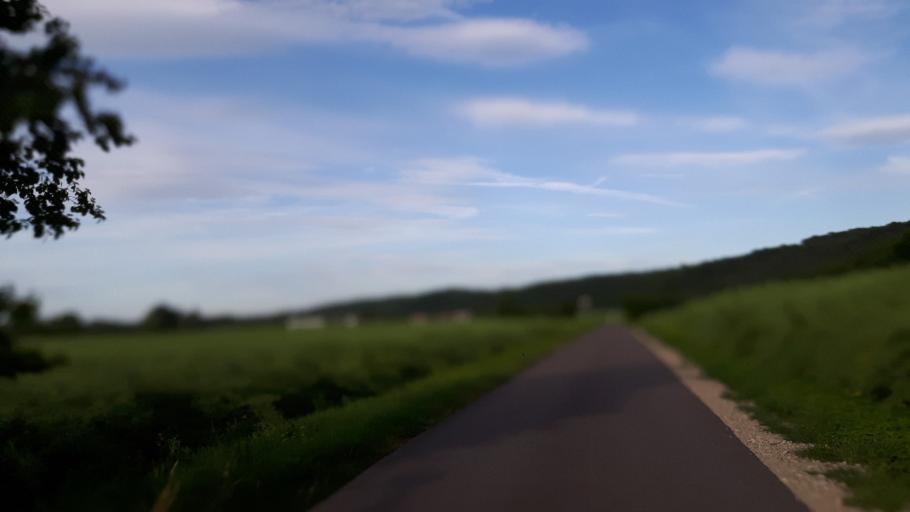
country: DE
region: Saxony-Anhalt
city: Leissling
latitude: 51.1783
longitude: 11.8873
